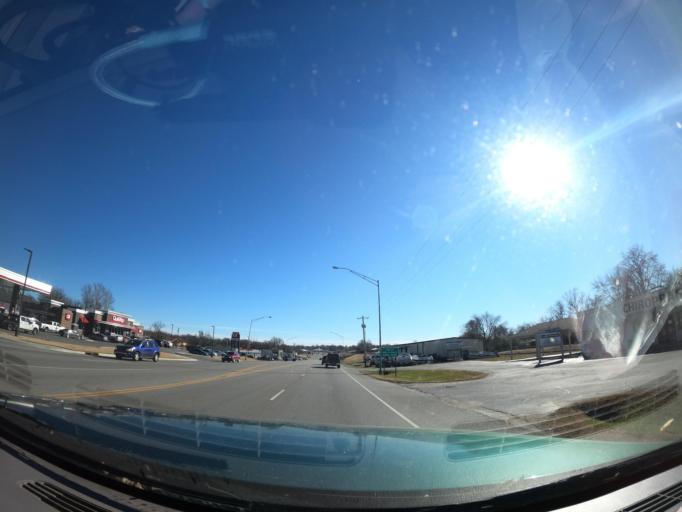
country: US
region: Oklahoma
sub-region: Wagoner County
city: Coweta
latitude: 35.9587
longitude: -95.6515
